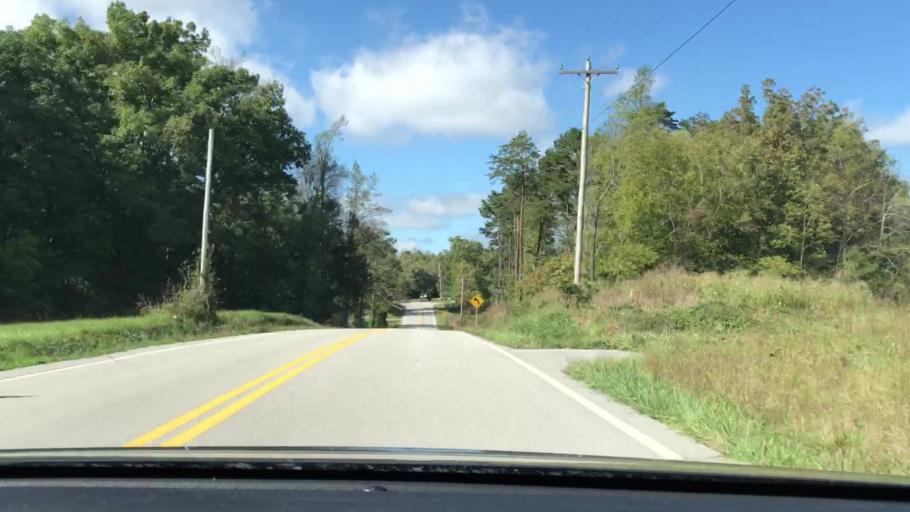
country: US
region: Tennessee
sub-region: Fentress County
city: Jamestown
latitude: 36.3706
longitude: -84.7599
